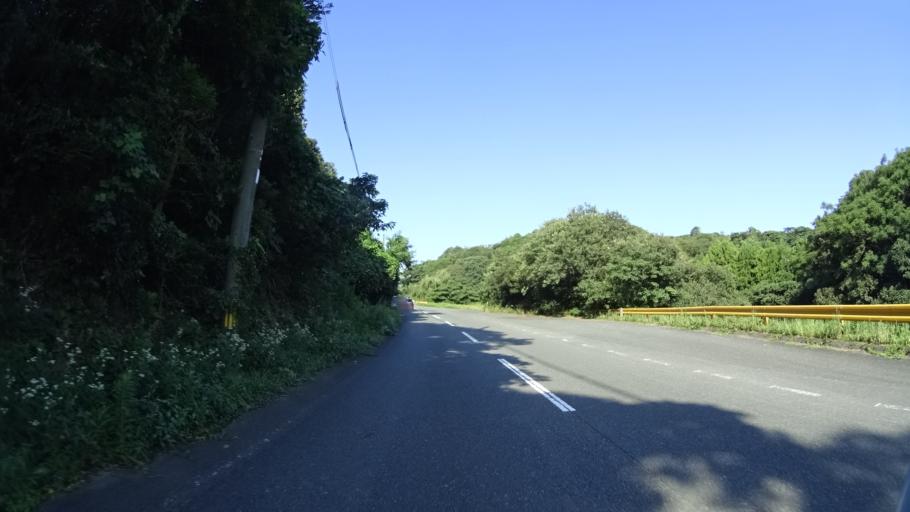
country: JP
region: Yamaguchi
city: Nagato
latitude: 34.3418
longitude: 130.9033
